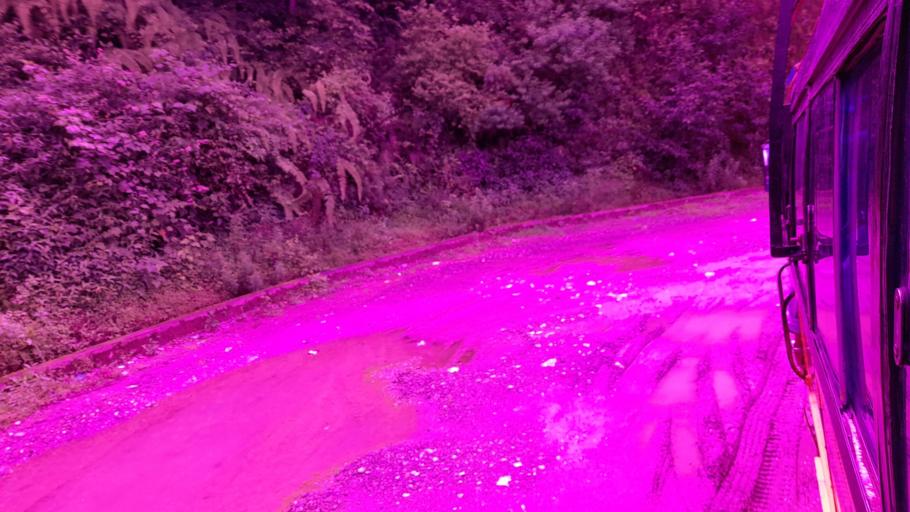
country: NP
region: Central Region
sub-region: Bagmati Zone
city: Kathmandu
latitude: 27.8173
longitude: 85.2454
